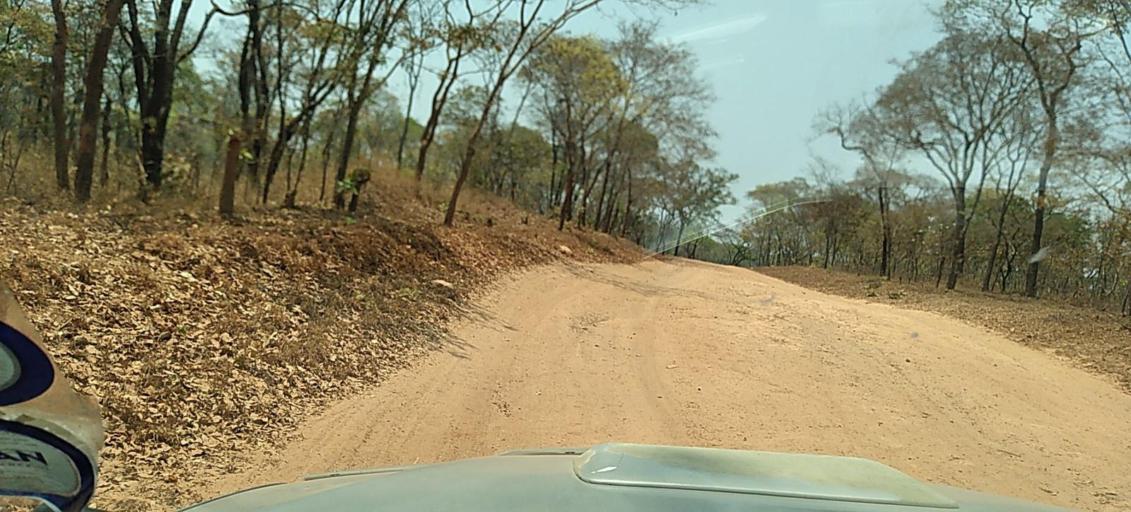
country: ZM
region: North-Western
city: Kasempa
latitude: -13.5491
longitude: 26.0615
